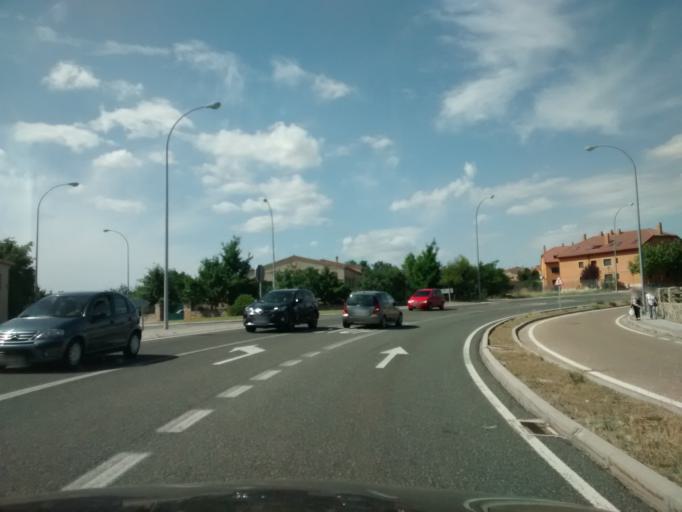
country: ES
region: Castille and Leon
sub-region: Provincia de Segovia
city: Torrecaballeros
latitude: 40.9945
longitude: -4.0222
